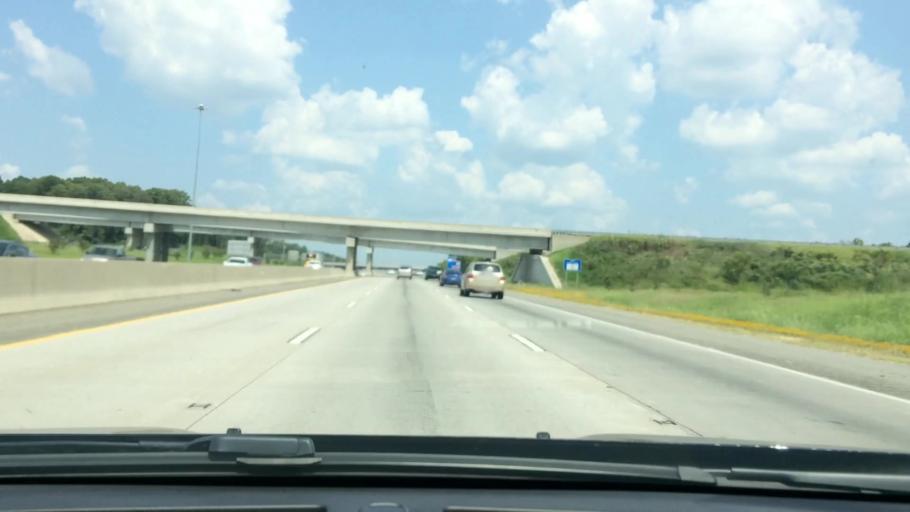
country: US
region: North Carolina
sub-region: Cabarrus County
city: Harrisburg
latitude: 35.3494
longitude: -80.7321
